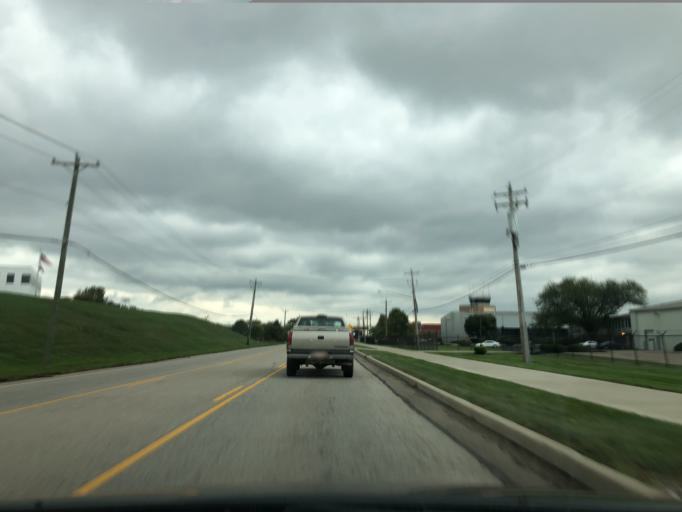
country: US
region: Kentucky
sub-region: Campbell County
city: Fort Thomas
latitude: 39.1067
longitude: -84.4260
